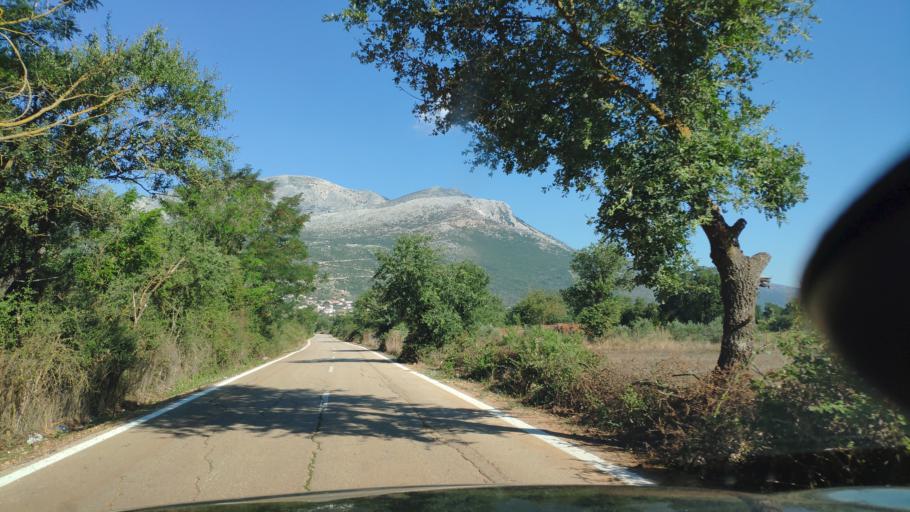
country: GR
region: West Greece
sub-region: Nomos Aitolias kai Akarnanias
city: Archontochorion
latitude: 38.6991
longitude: 21.0969
